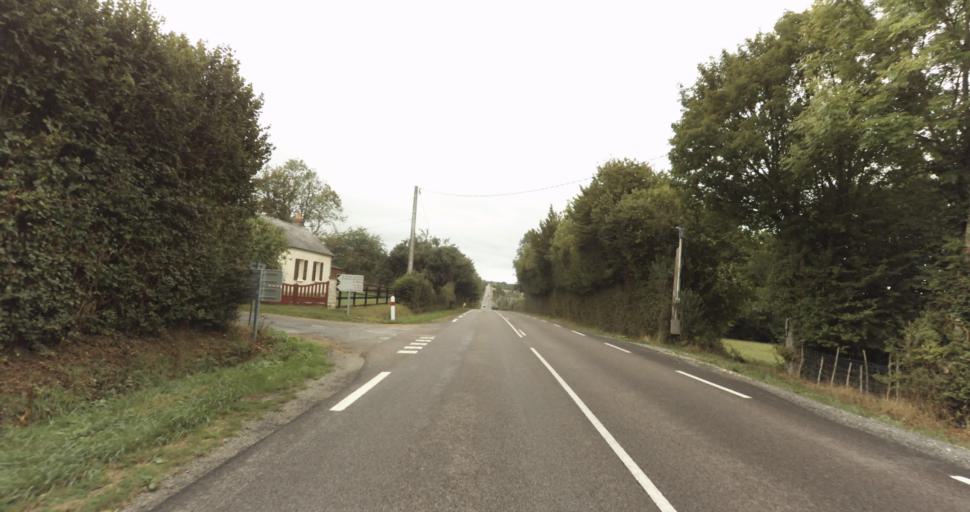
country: FR
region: Lower Normandy
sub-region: Departement de l'Orne
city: Sainte-Gauburge-Sainte-Colombe
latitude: 48.7243
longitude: 0.4592
